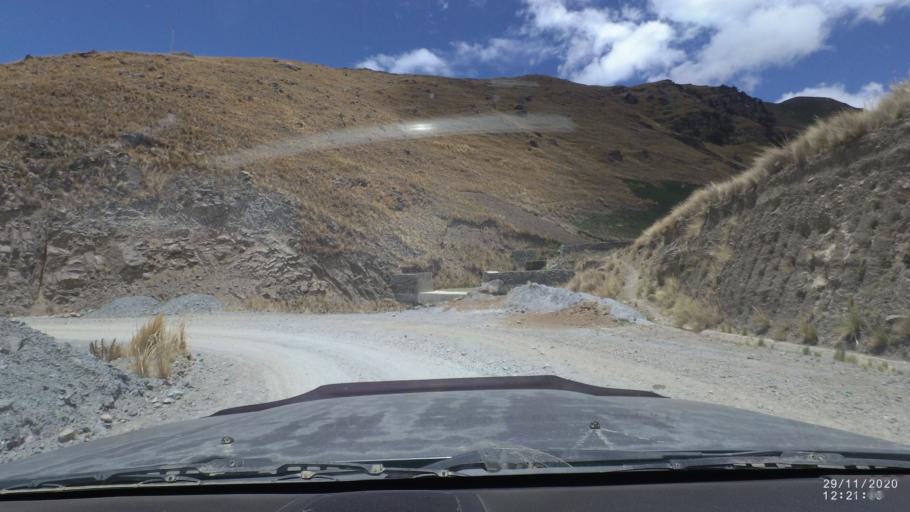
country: BO
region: Cochabamba
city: Cochabamba
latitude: -17.0981
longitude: -66.3202
